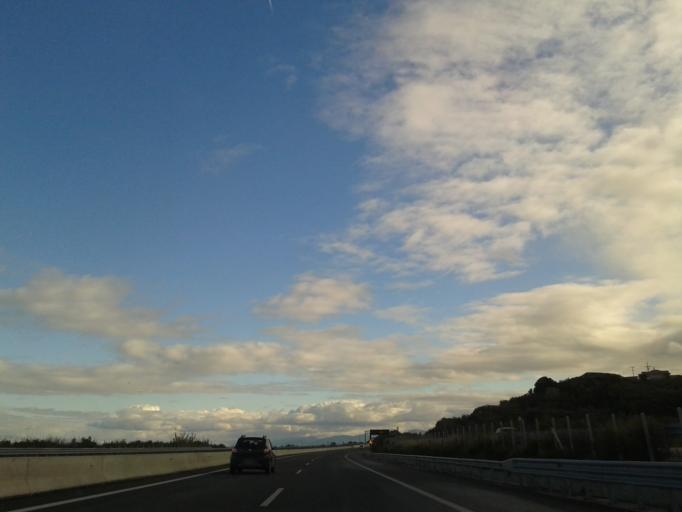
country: GR
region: Peloponnese
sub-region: Nomos Korinthias
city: Kato Dhiminio
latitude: 38.0316
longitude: 22.7178
